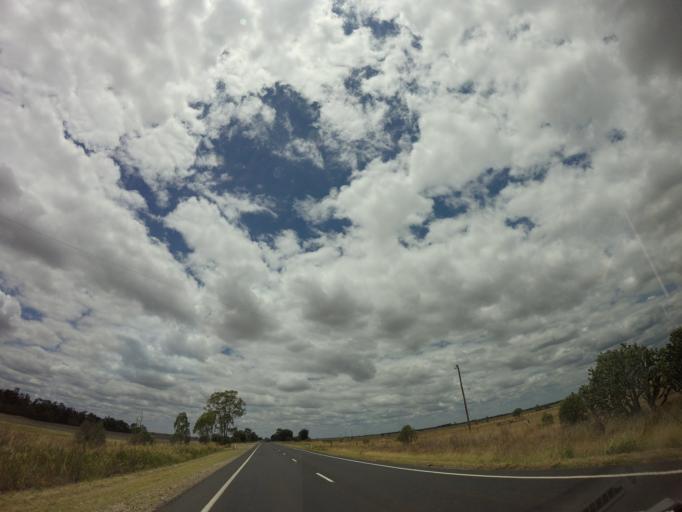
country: AU
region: Queensland
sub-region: Goondiwindi
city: Goondiwindi
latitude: -28.1736
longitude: 150.4924
